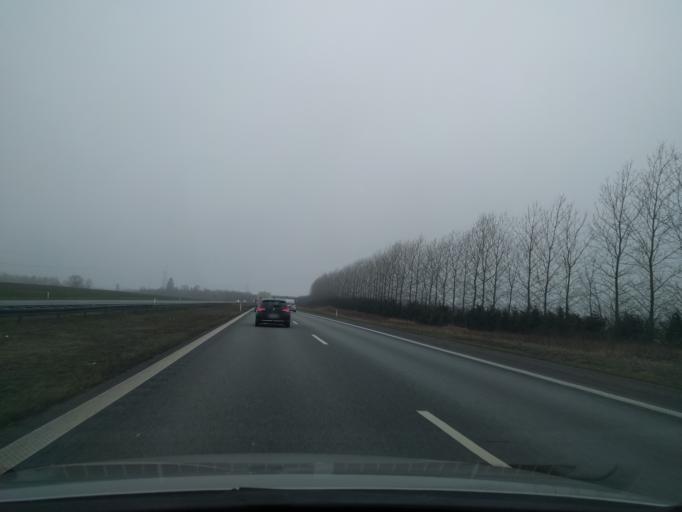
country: DK
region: Zealand
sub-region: Ringsted Kommune
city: Ringsted
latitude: 55.4518
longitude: 11.8810
